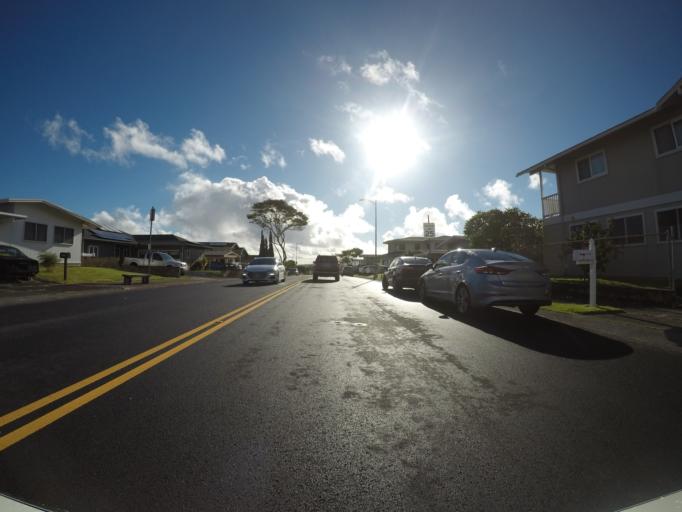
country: US
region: Hawaii
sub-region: Honolulu County
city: He'eia
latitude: 21.4244
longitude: -157.8078
